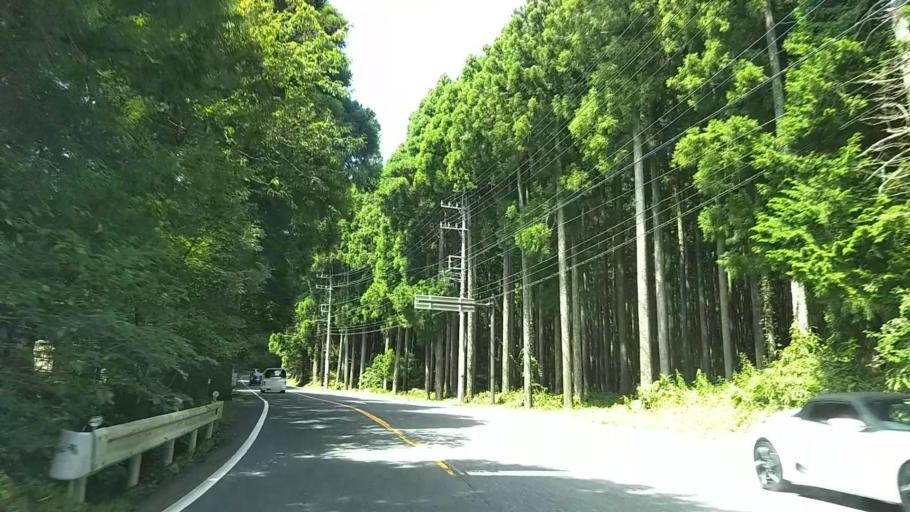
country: JP
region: Shizuoka
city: Gotemba
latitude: 35.2585
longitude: 138.8240
